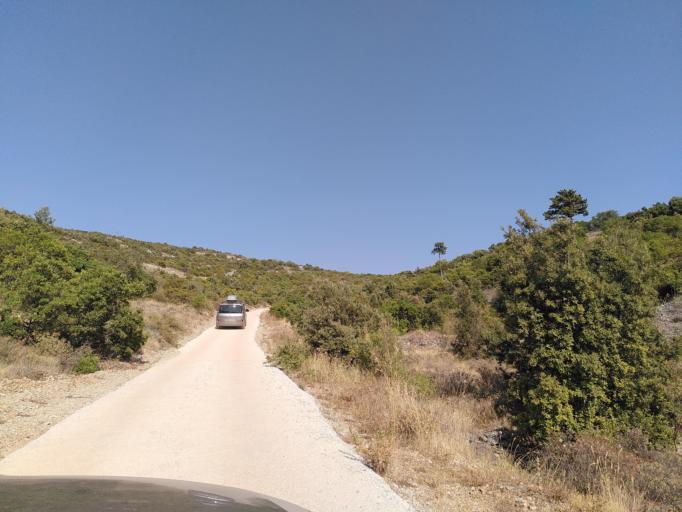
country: HR
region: Splitsko-Dalmatinska
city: Stari Grad
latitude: 43.1538
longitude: 16.5796
